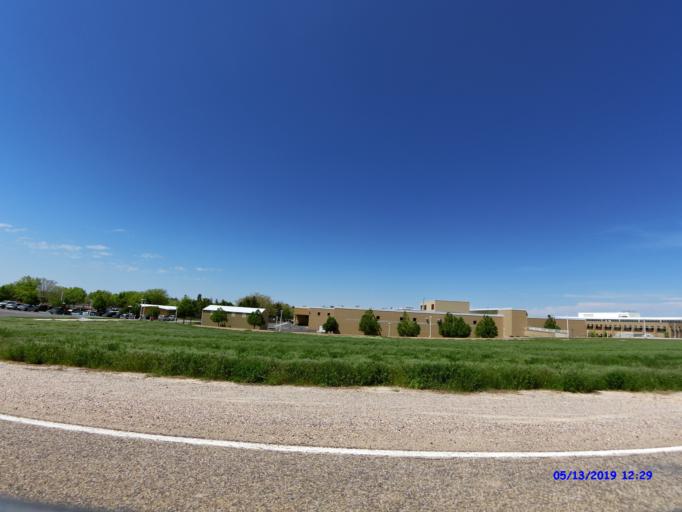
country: US
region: Utah
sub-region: Weber County
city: Harrisville
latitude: 41.2633
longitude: -111.9604
